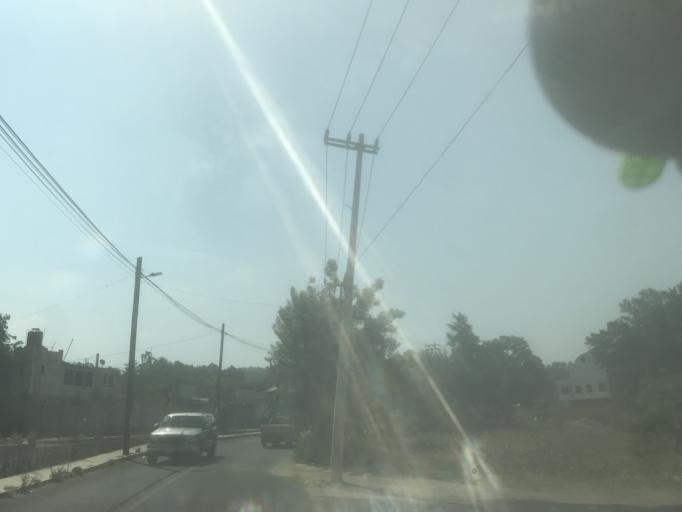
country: MX
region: Mexico
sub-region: Atlautla
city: San Juan Tepecoculco
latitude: 18.9917
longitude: -98.7926
